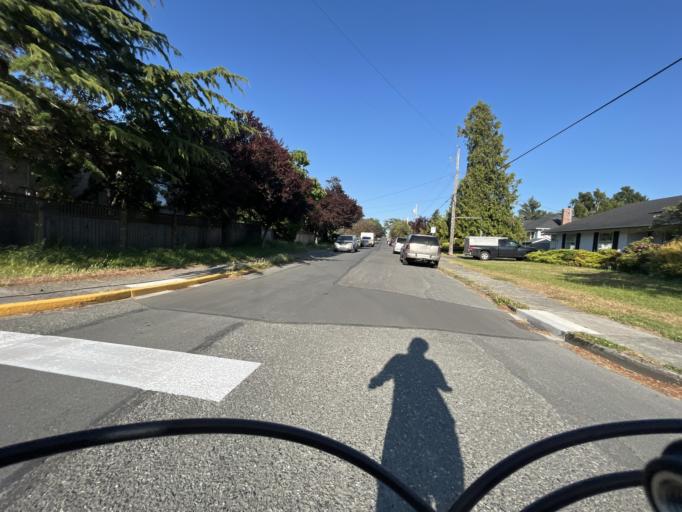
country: CA
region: British Columbia
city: Oak Bay
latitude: 48.4377
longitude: -123.3221
